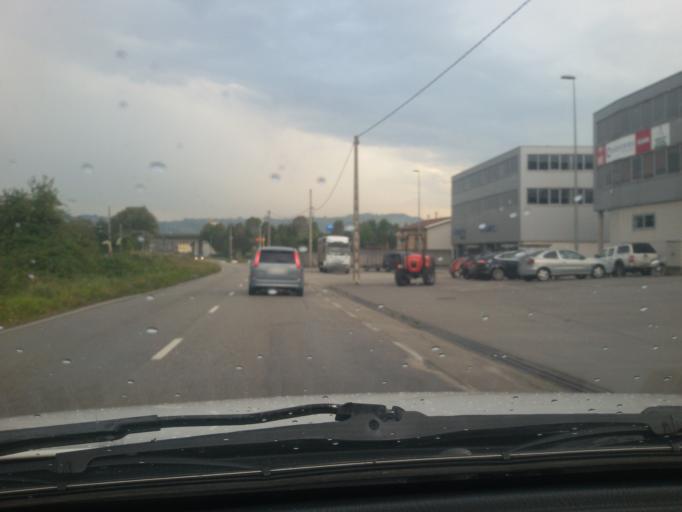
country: ES
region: Asturias
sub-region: Province of Asturias
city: Lugones
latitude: 43.3949
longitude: -5.7893
